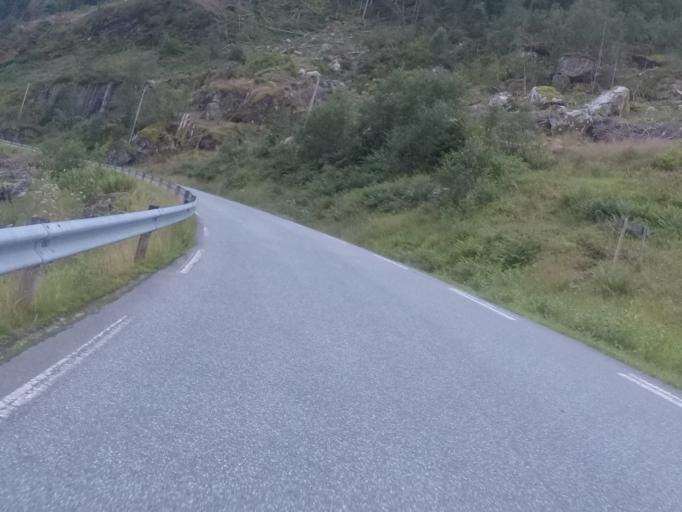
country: NO
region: Sogn og Fjordane
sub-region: Balestrand
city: Balestrand
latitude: 61.2758
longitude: 6.5000
